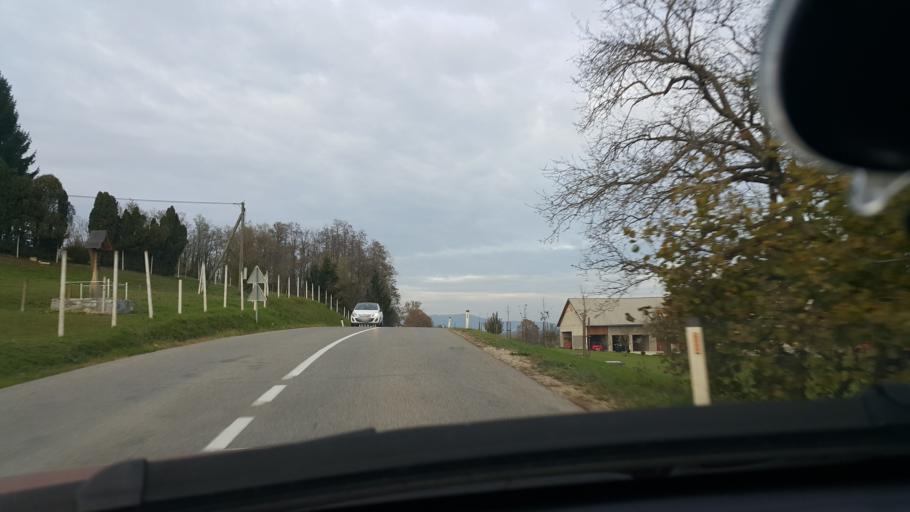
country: SI
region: Bistrica ob Sotli
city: Bistrica ob Sotli
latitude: 45.9664
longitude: 15.6934
